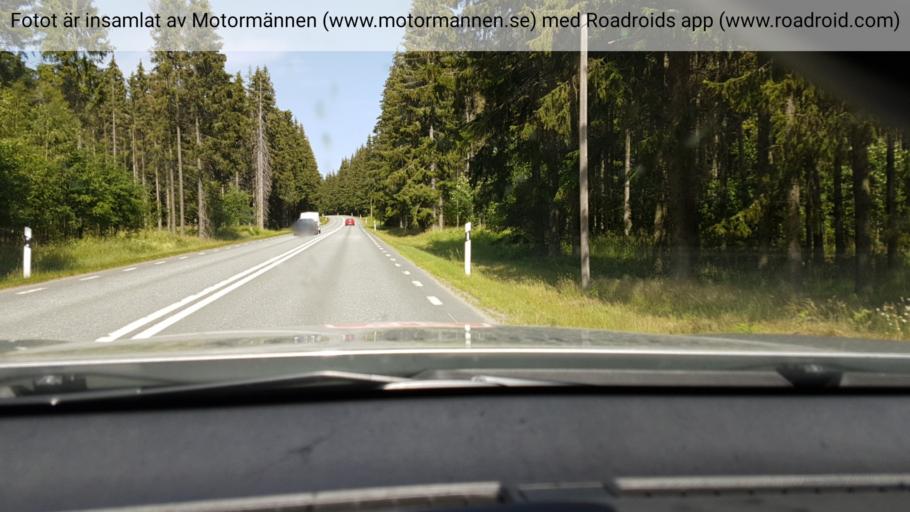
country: SE
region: Joenkoeping
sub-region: Nassjo Kommun
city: Bodafors
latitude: 57.5552
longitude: 14.8010
